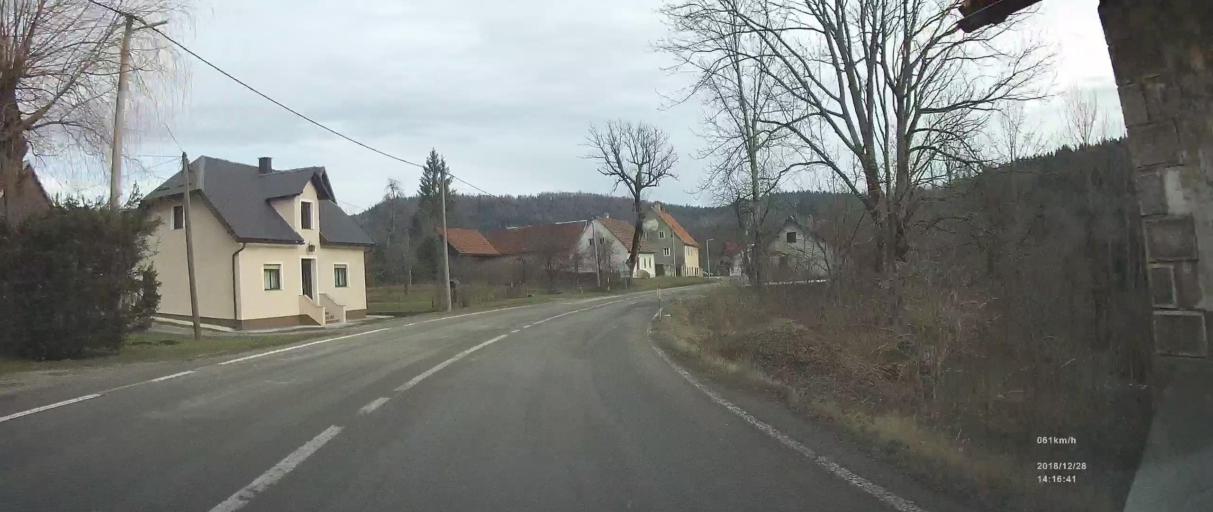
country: HR
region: Primorsko-Goranska
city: Vrbovsko
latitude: 45.4179
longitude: 15.0385
